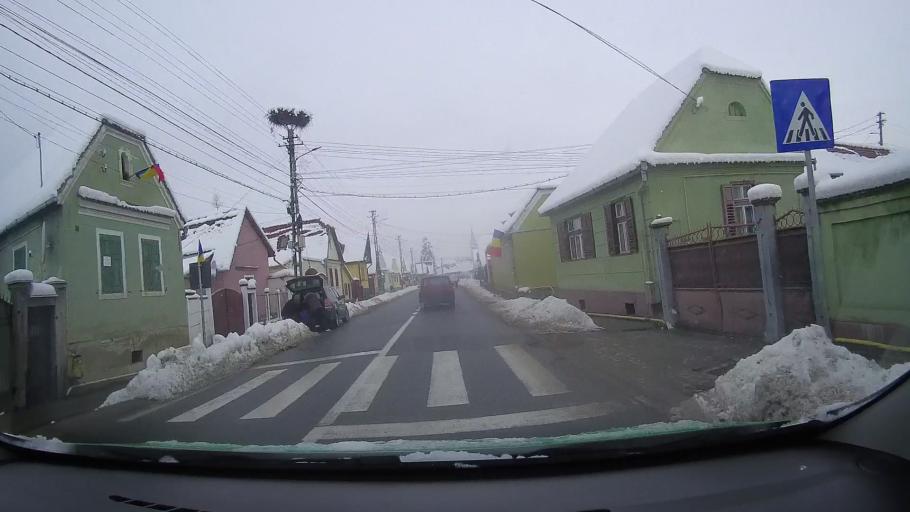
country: RO
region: Sibiu
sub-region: Comuna Cristian
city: Cristian
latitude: 45.7786
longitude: 24.0278
